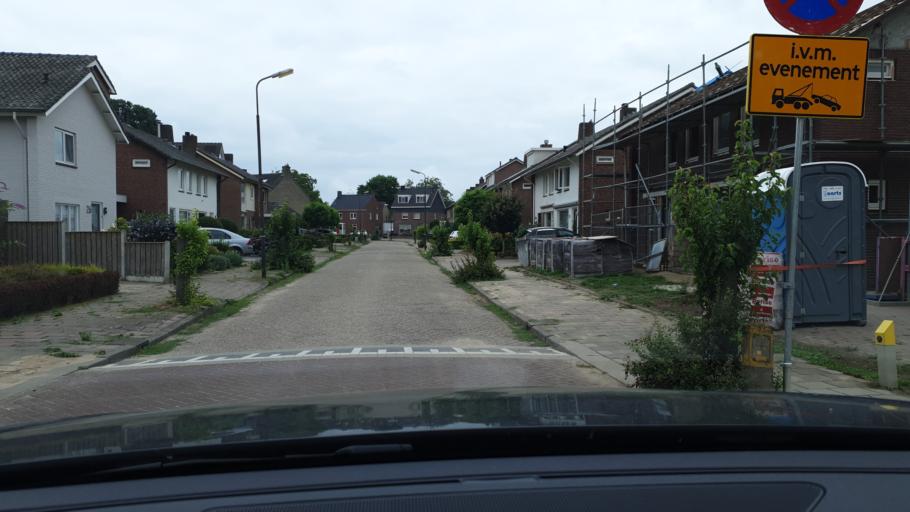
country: NL
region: North Brabant
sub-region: Gemeente Veldhoven
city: Veldhoven
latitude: 51.4256
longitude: 5.4115
